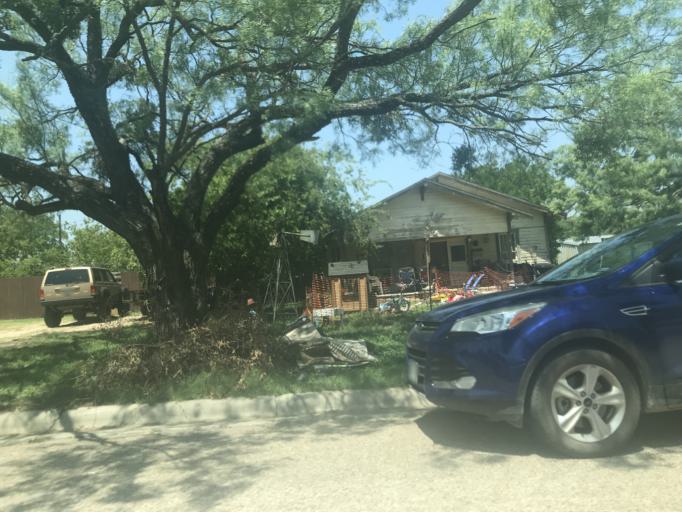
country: US
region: Texas
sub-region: Taylor County
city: Abilene
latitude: 32.4460
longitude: -99.7512
